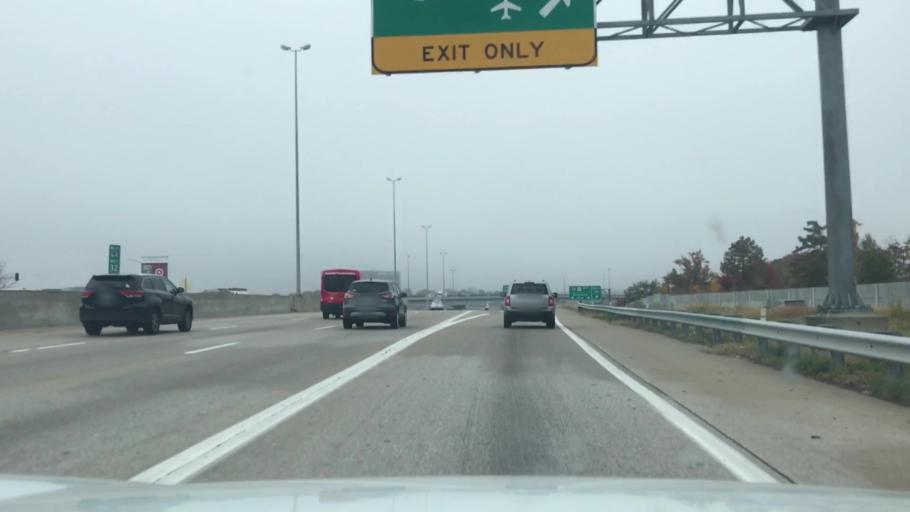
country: US
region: Missouri
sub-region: Saint Louis County
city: Brentwood
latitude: 38.6299
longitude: -90.3384
